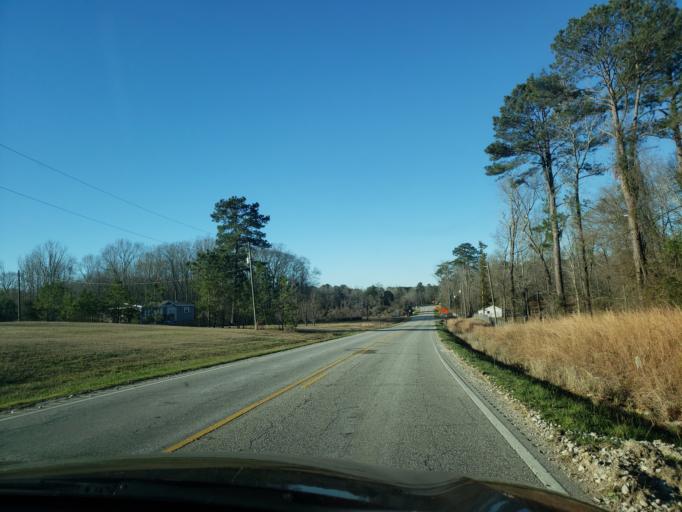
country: US
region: Alabama
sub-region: Macon County
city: Tuskegee
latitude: 32.5740
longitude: -85.6581
